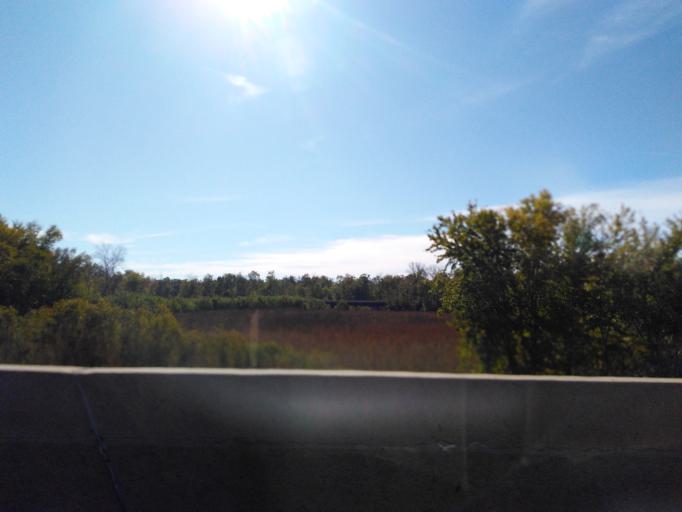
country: US
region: Illinois
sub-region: Bond County
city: Greenville
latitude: 38.8363
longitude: -89.5050
